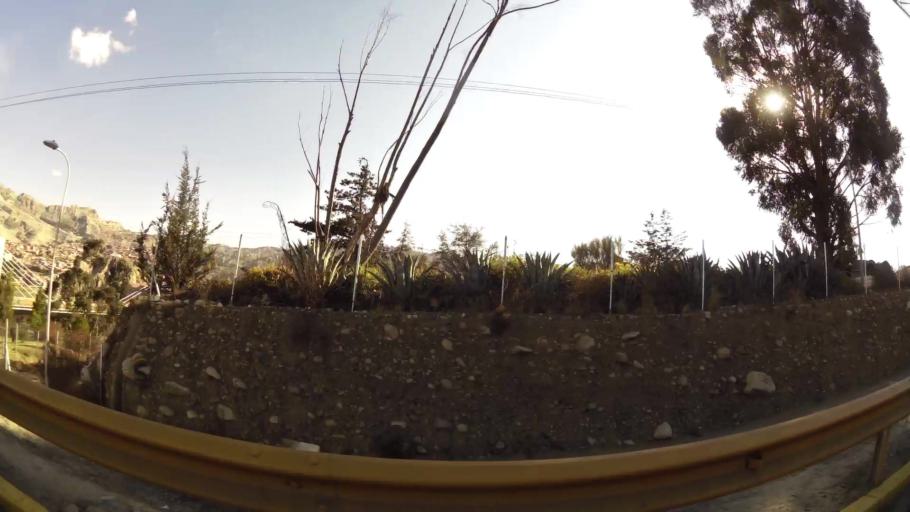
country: BO
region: La Paz
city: La Paz
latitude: -16.5150
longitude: -68.1167
